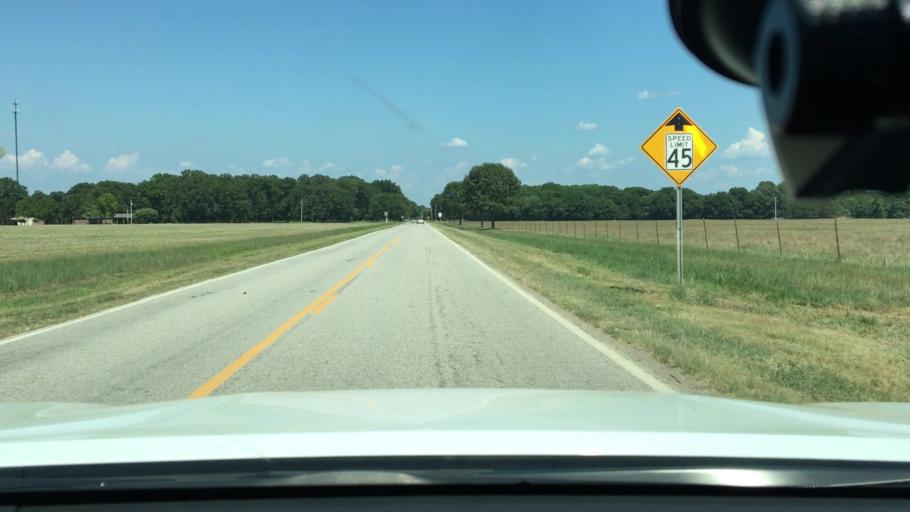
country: US
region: Arkansas
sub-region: Johnson County
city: Coal Hill
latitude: 35.3575
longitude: -93.5570
